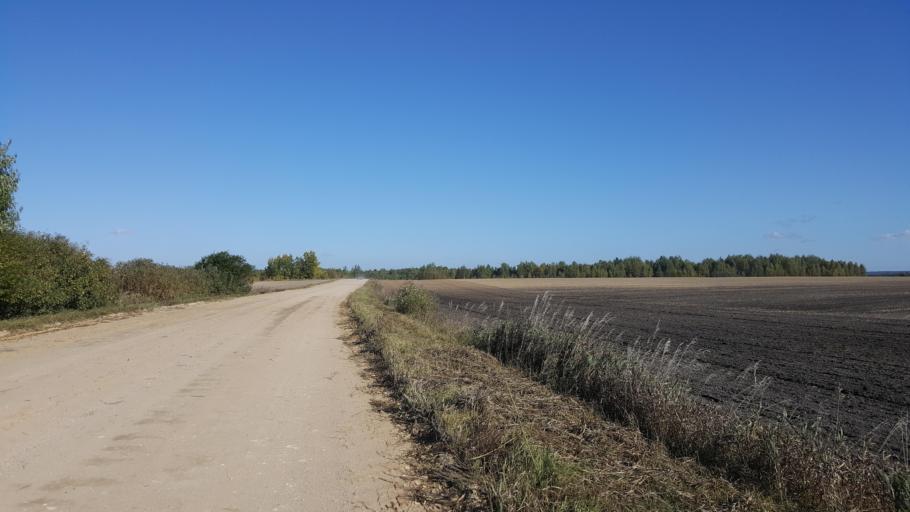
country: BY
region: Brest
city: Kamyanyets
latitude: 52.4305
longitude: 23.8828
